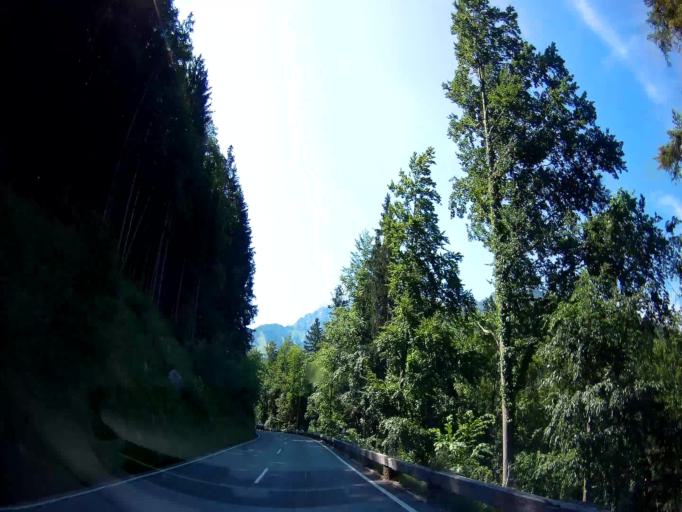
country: DE
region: Bavaria
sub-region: Upper Bavaria
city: Berchtesgaden
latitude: 47.6369
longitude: 13.0542
